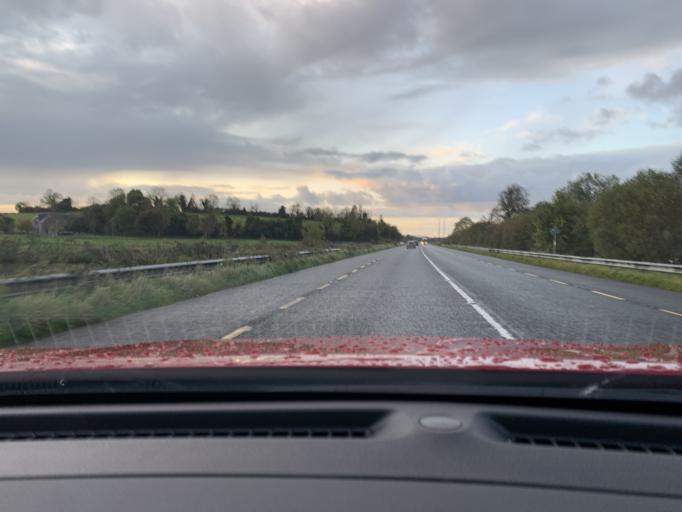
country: IE
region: Connaught
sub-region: County Leitrim
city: Carrick-on-Shannon
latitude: 53.9456
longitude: -8.1182
